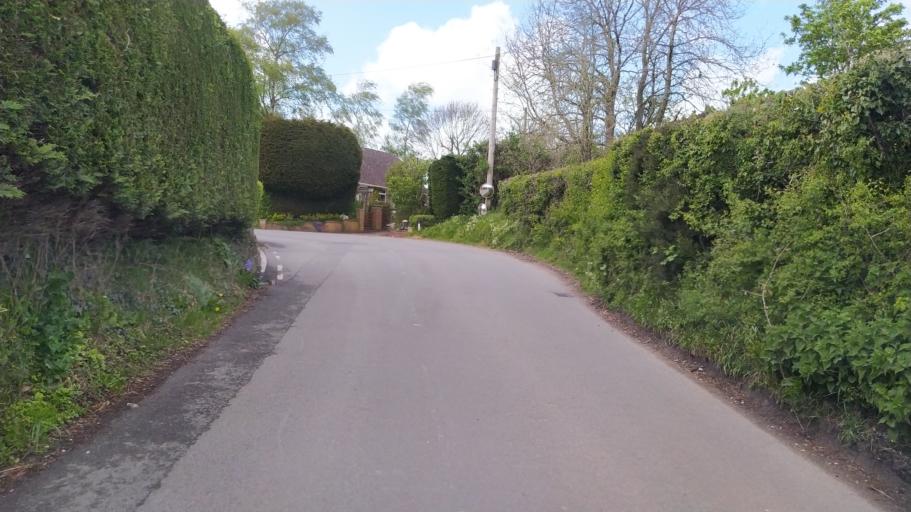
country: GB
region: England
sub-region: Dorset
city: Sturminster Newton
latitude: 50.8980
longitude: -2.2742
